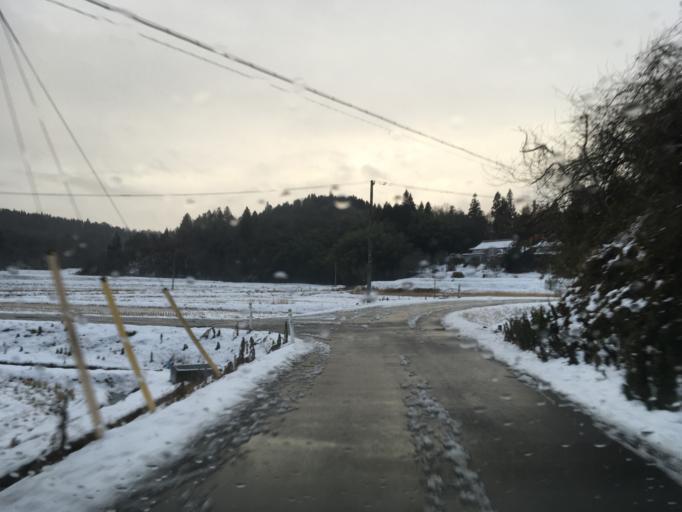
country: JP
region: Iwate
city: Ichinoseki
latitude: 38.8853
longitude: 141.2367
